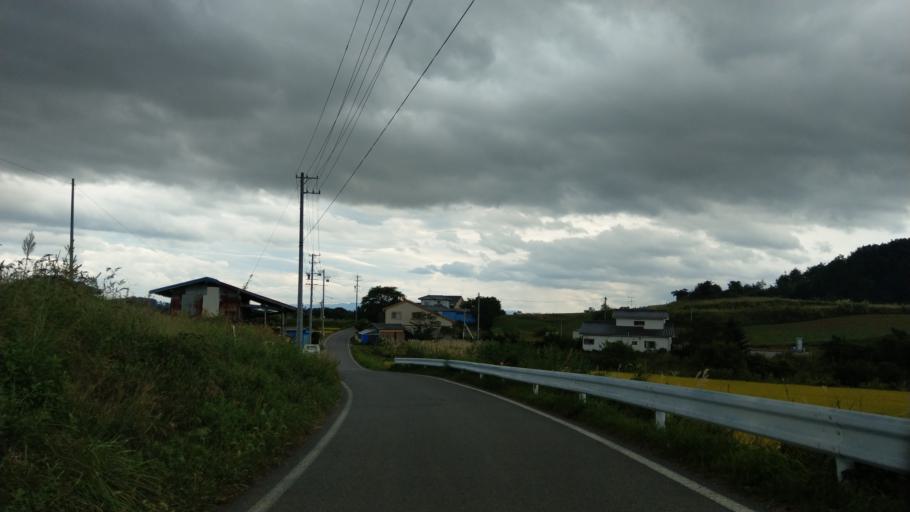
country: JP
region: Nagano
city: Komoro
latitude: 36.3146
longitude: 138.3917
